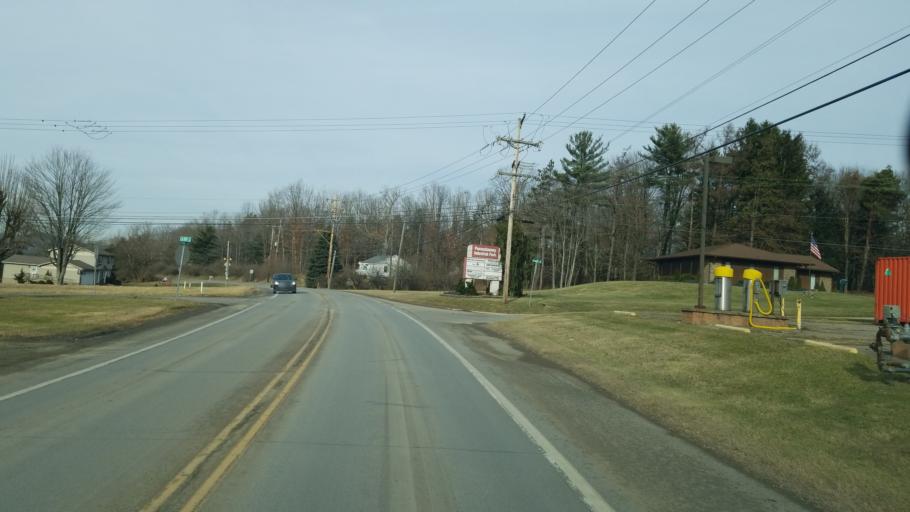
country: US
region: Pennsylvania
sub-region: Jefferson County
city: Punxsutawney
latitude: 40.9328
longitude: -78.9878
